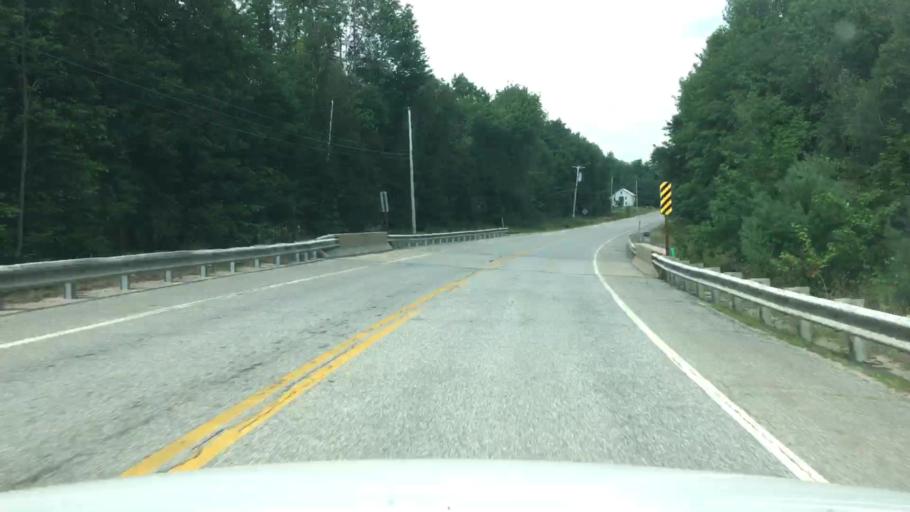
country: US
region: Maine
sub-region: Oxford County
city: Rumford
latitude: 44.5591
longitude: -70.7157
